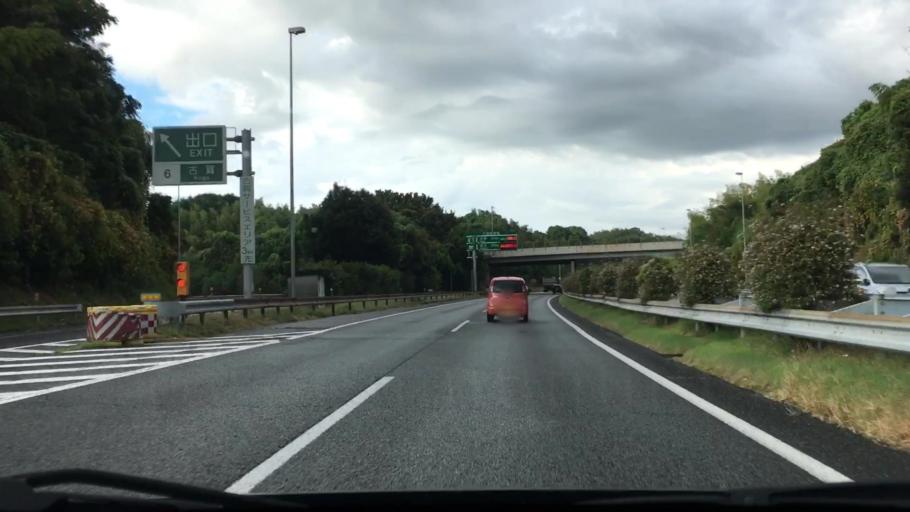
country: JP
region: Fukuoka
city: Koga
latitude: 33.7176
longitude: 130.4922
